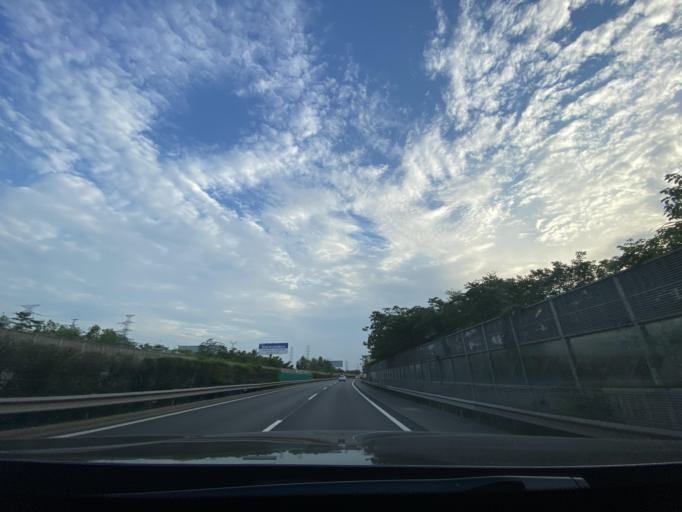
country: CN
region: Sichuan
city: Deyang
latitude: 31.0863
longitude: 104.4089
